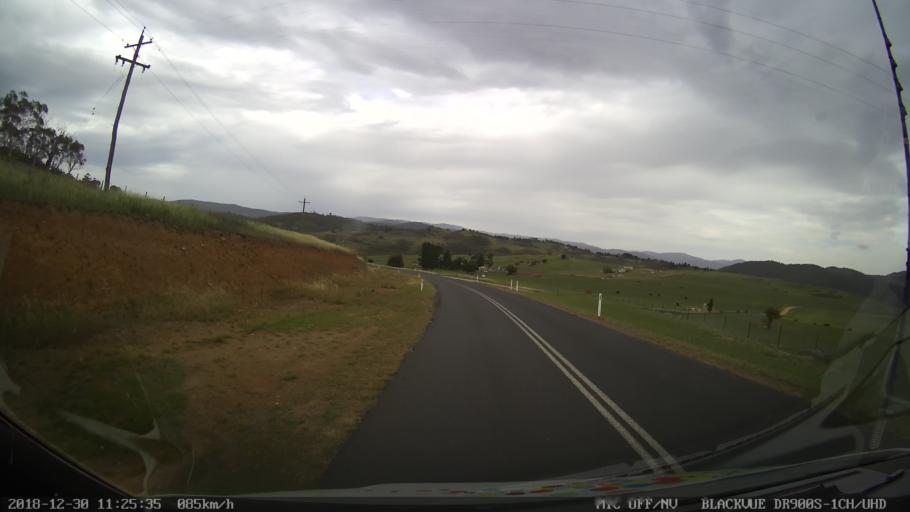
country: AU
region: New South Wales
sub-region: Snowy River
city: Jindabyne
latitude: -36.4697
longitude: 148.6464
